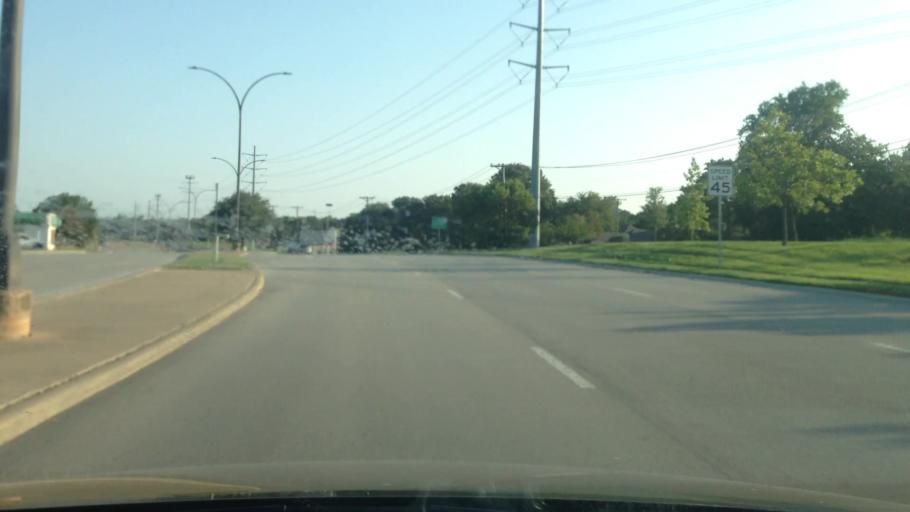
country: US
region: Texas
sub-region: Tarrant County
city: Pantego
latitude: 32.7101
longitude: -97.1907
